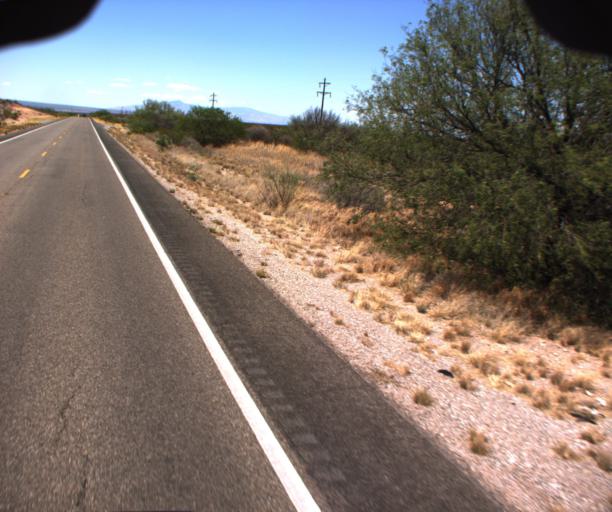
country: US
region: Arizona
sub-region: Cochise County
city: Tombstone
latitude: 31.7801
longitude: -110.1375
